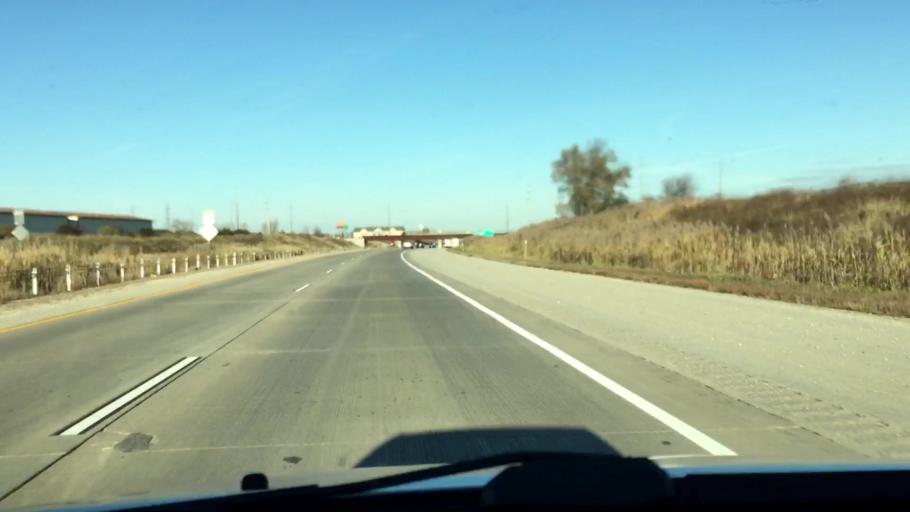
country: US
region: Wisconsin
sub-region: Fond du Lac County
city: Fond du Lac
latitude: 43.7463
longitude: -88.4554
